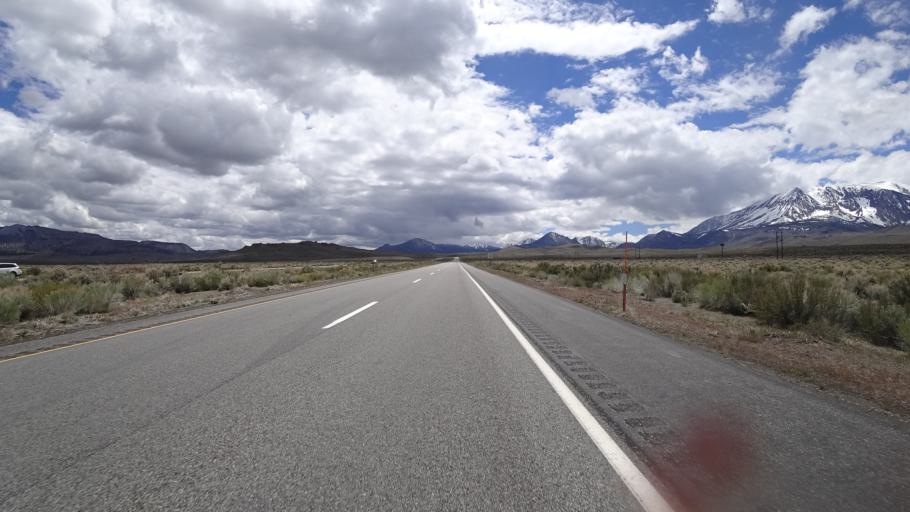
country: US
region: California
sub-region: Mono County
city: Mammoth Lakes
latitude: 37.8785
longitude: -119.0897
